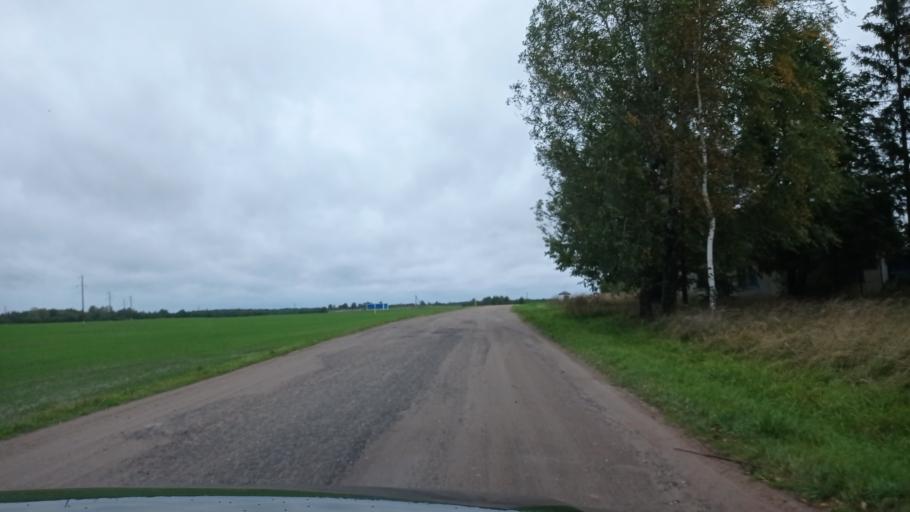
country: BY
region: Vitebsk
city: Haradok
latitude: 55.3381
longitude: 30.0945
